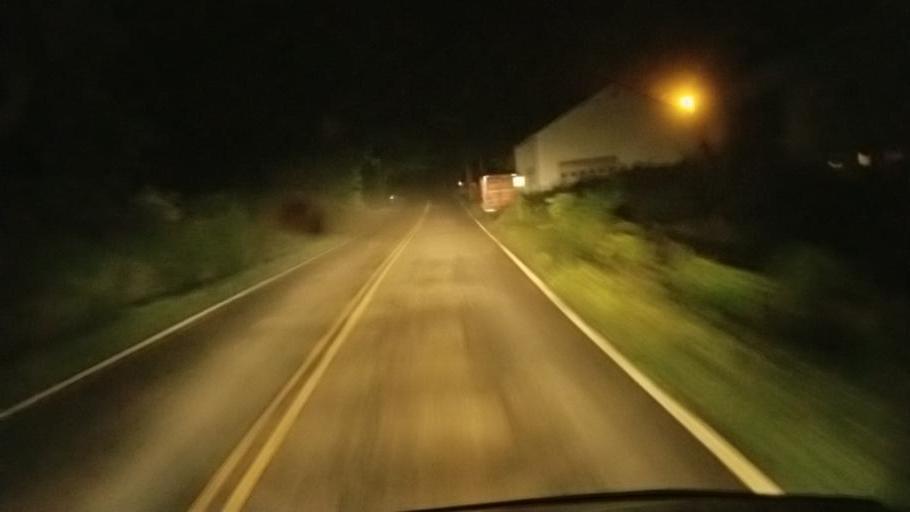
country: US
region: Ohio
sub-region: Coshocton County
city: Coshocton
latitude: 40.3529
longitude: -82.0186
